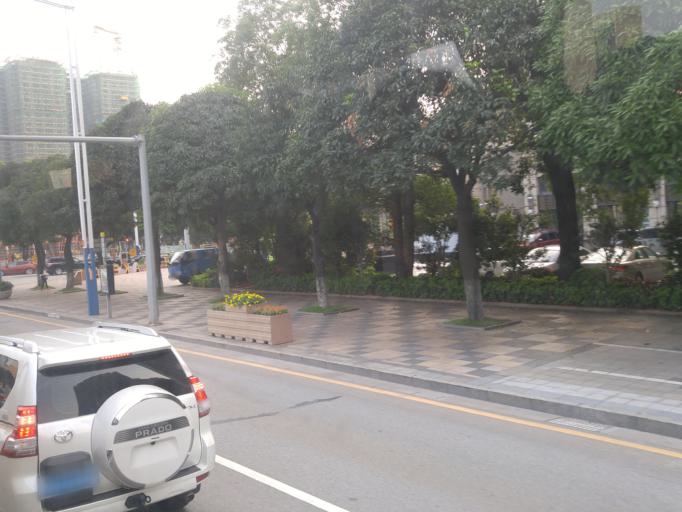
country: CN
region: Guangdong
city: Foshan
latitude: 23.0664
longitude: 113.1404
